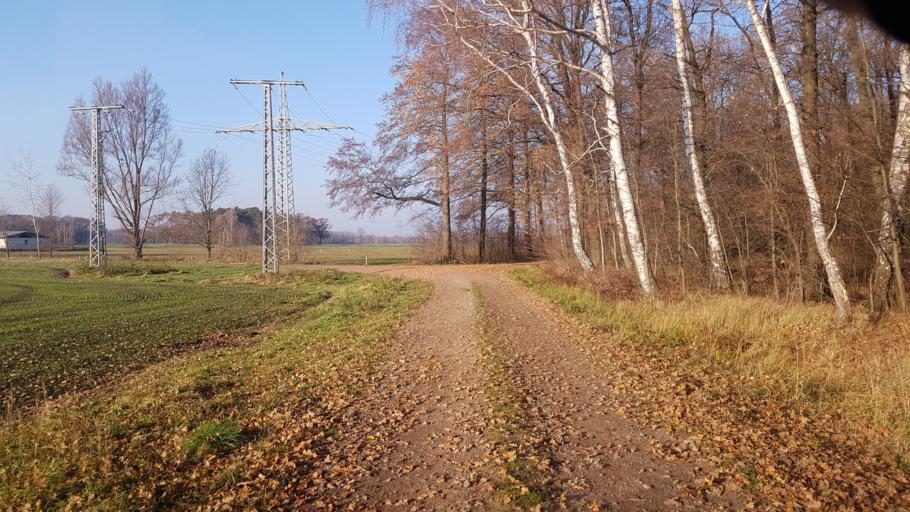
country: DE
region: Brandenburg
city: Tettau
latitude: 51.4410
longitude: 13.7282
